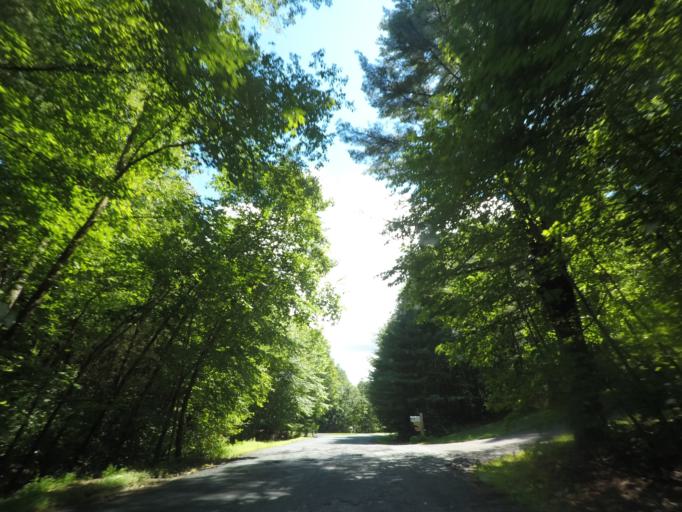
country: US
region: New York
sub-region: Rensselaer County
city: Averill Park
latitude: 42.6280
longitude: -73.5779
